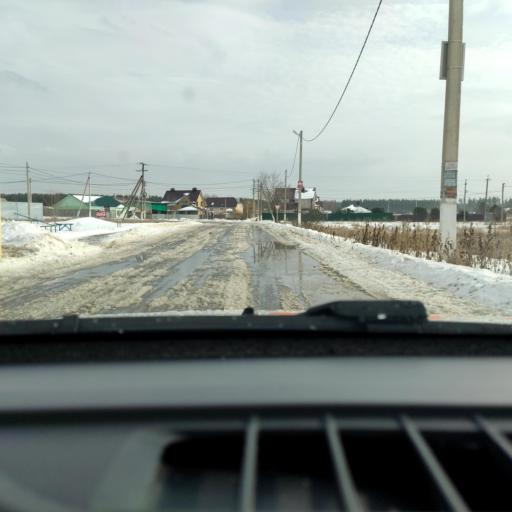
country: RU
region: Voronezj
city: Podgornoye
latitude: 51.7739
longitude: 39.1238
